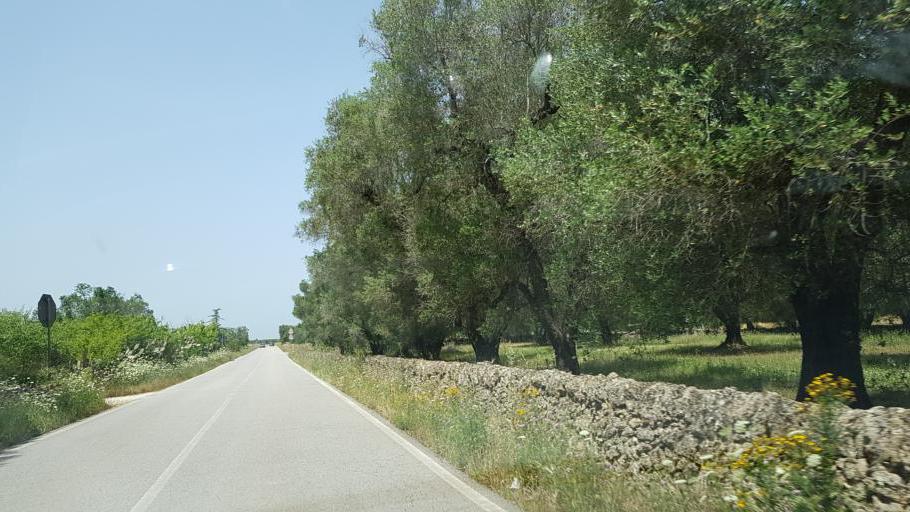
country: IT
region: Apulia
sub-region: Provincia di Brindisi
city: Mesagne
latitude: 40.5178
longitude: 17.8250
